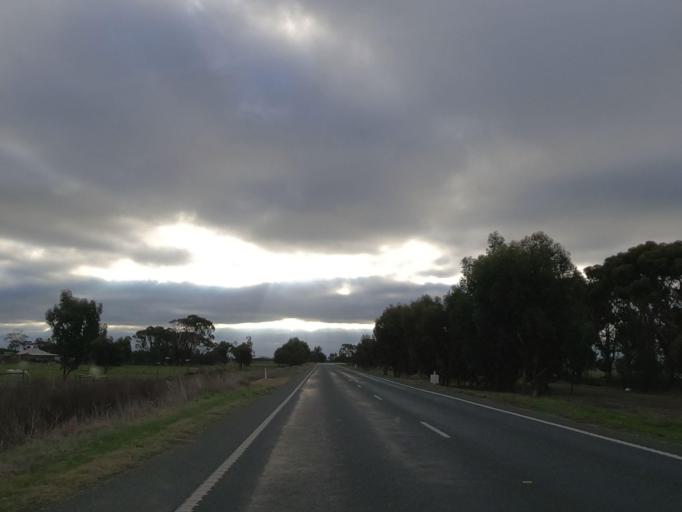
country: AU
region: Victoria
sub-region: Swan Hill
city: Swan Hill
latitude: -35.7315
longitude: 143.8954
